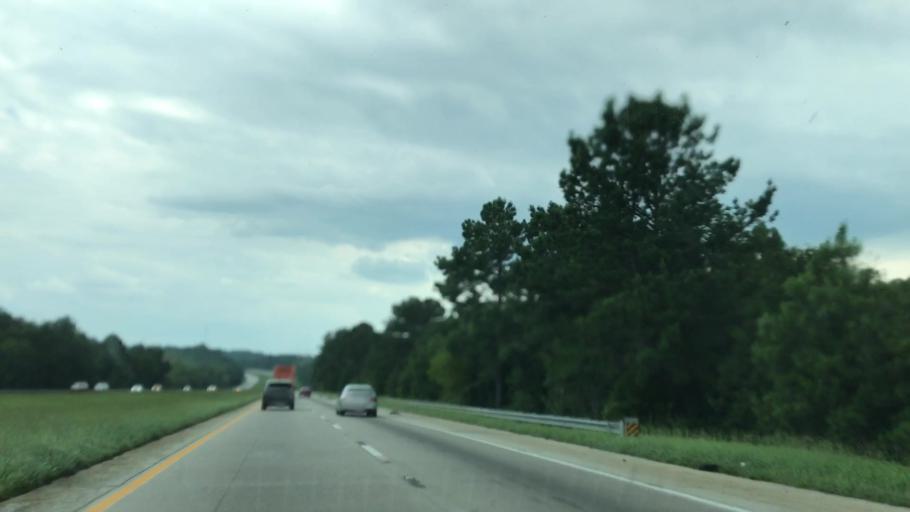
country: US
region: South Carolina
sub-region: Fairfield County
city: Winnsboro Mills
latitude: 34.3343
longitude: -81.0043
